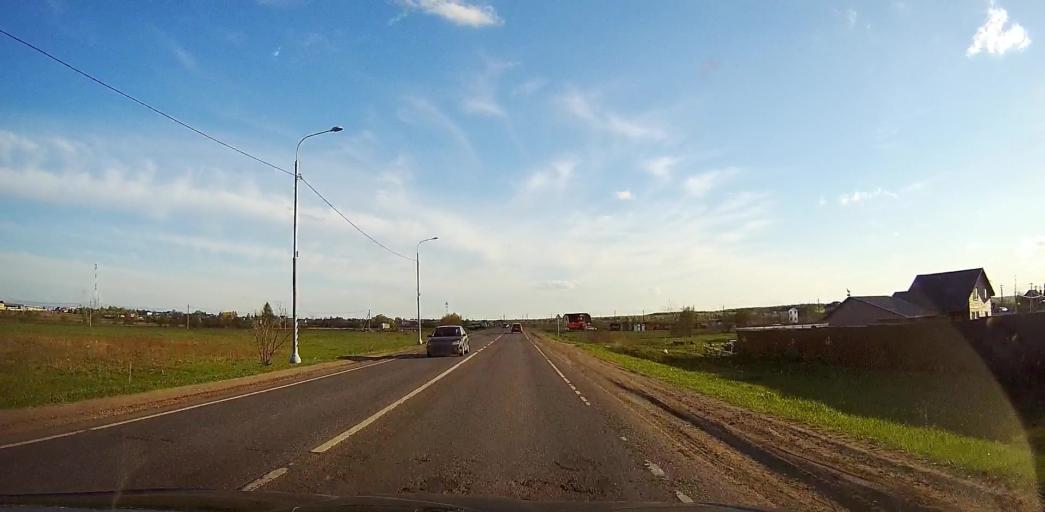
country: RU
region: Moskovskaya
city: Bronnitsy
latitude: 55.3364
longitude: 38.2212
